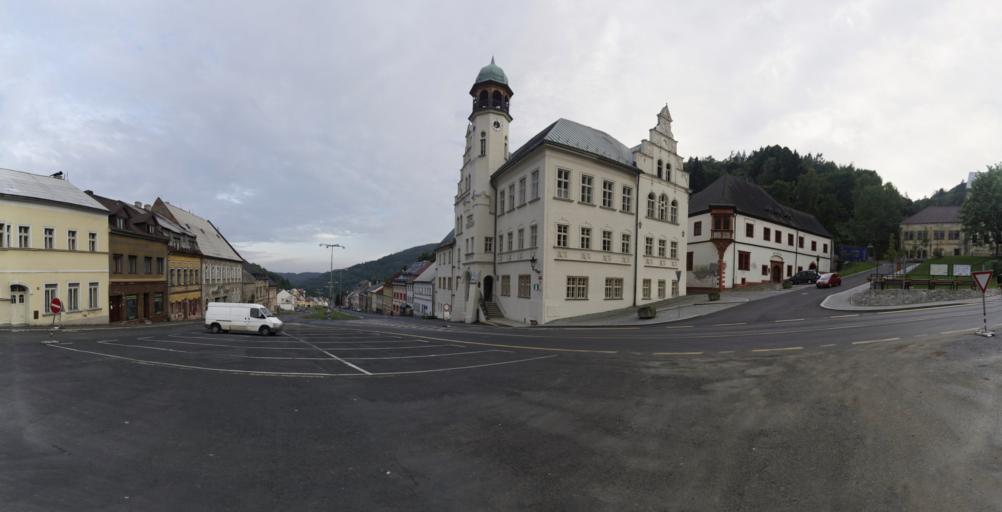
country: CZ
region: Karlovarsky
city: Jachymov
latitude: 50.3718
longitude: 12.9135
